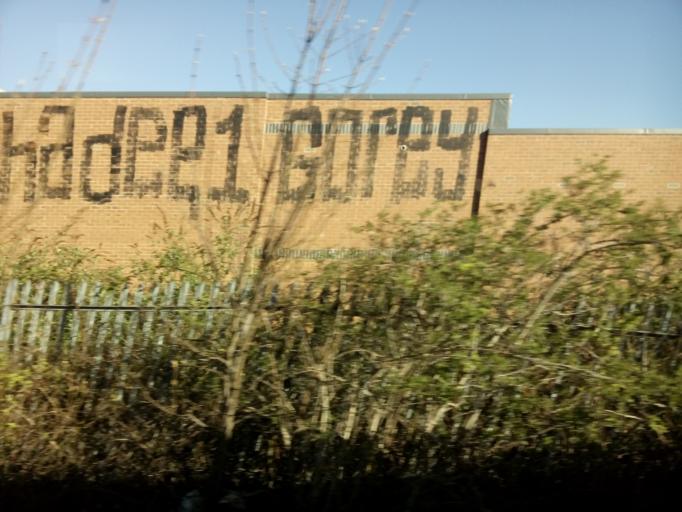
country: GB
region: England
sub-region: Gateshead
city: Gateshead
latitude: 54.9756
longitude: -1.5961
